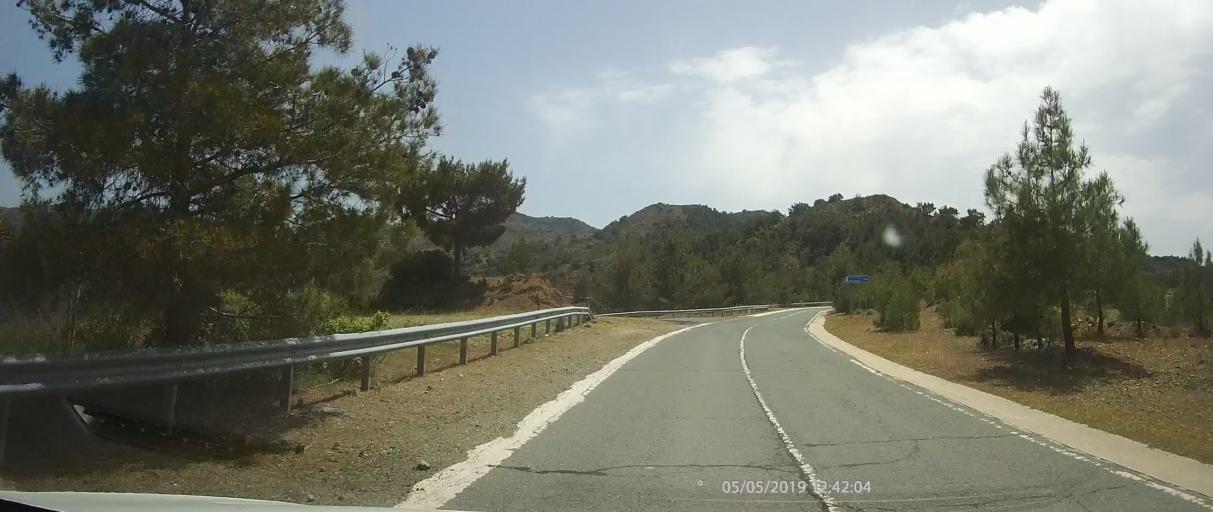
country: CY
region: Lefkosia
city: Kakopetria
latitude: 34.9771
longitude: 32.8097
